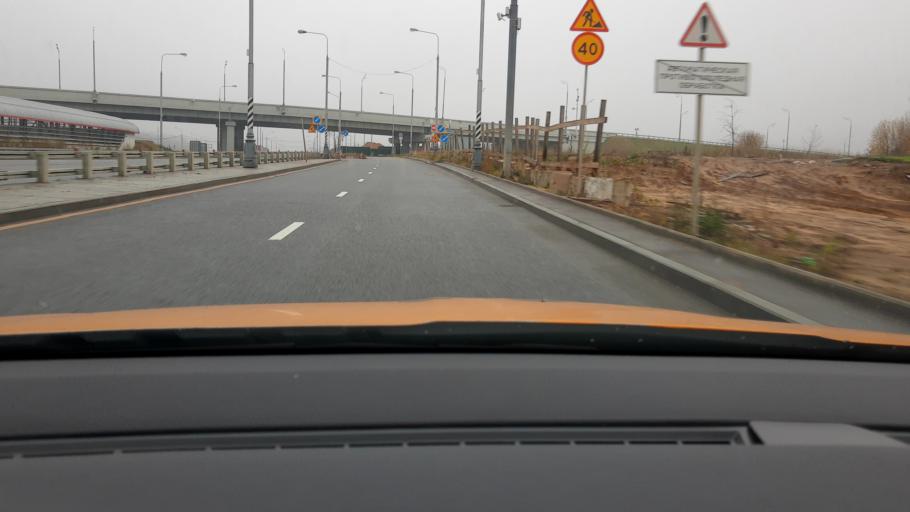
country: RU
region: Moskovskaya
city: Kommunarka
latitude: 55.5631
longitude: 37.4640
